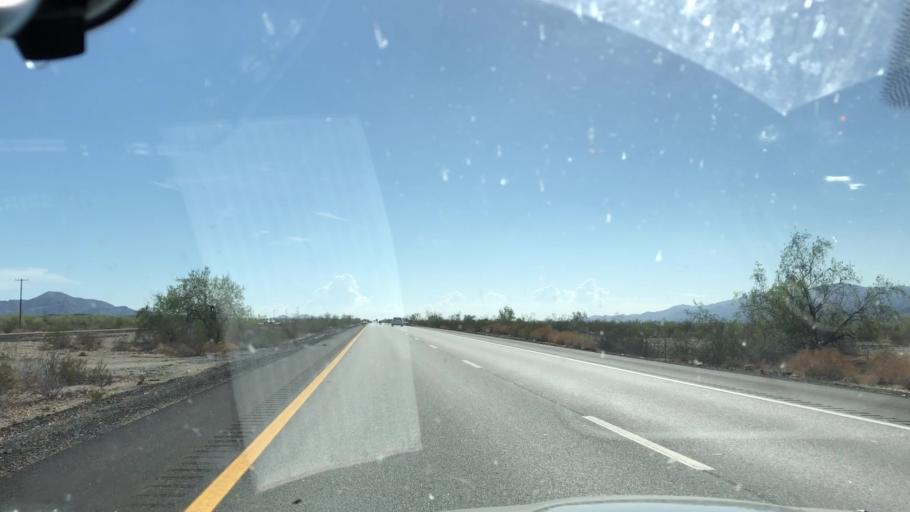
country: US
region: California
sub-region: Imperial County
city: Niland
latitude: 33.6924
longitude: -115.4985
